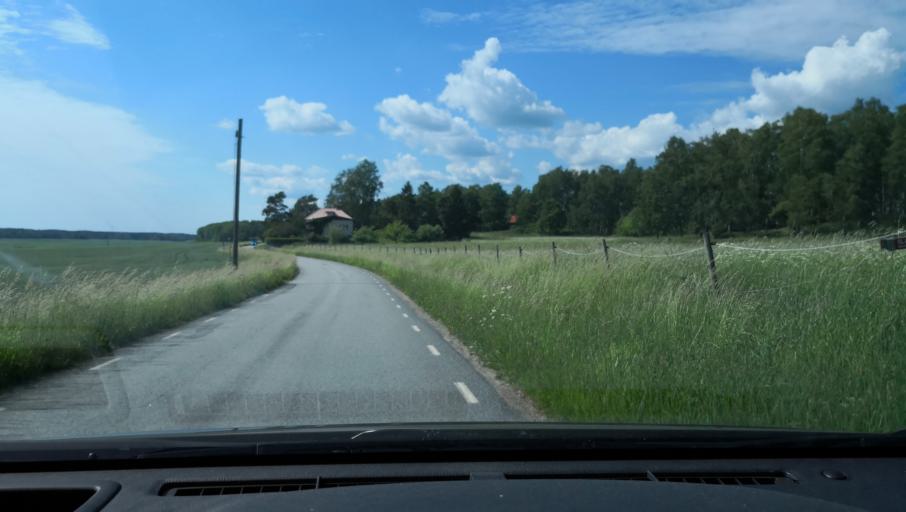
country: SE
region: Uppsala
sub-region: Enkopings Kommun
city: Orsundsbro
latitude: 59.8170
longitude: 17.3350
